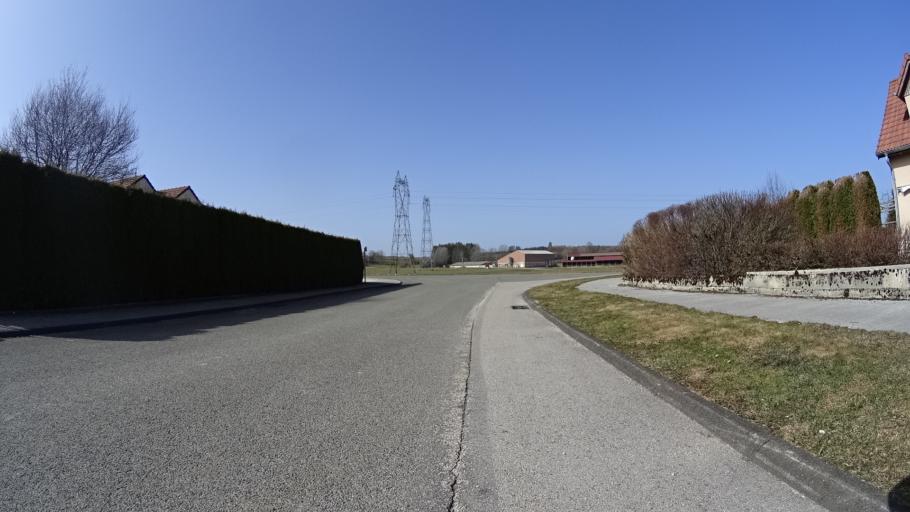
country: FR
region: Franche-Comte
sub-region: Departement du Doubs
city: Frasne
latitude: 46.8518
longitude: 6.1464
